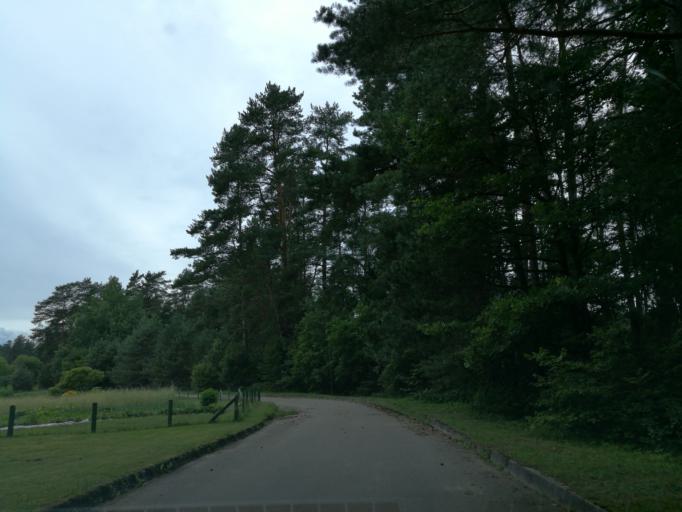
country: LT
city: Grigiskes
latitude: 54.7200
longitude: 25.0488
